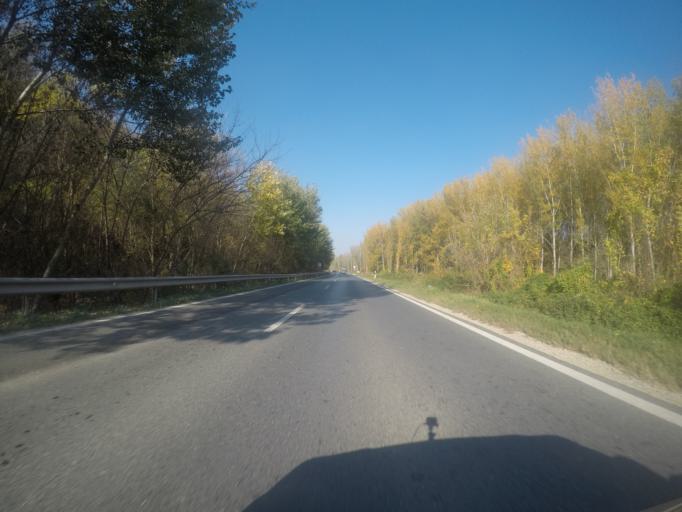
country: HU
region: Tolna
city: Paks
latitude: 46.6507
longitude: 18.8825
